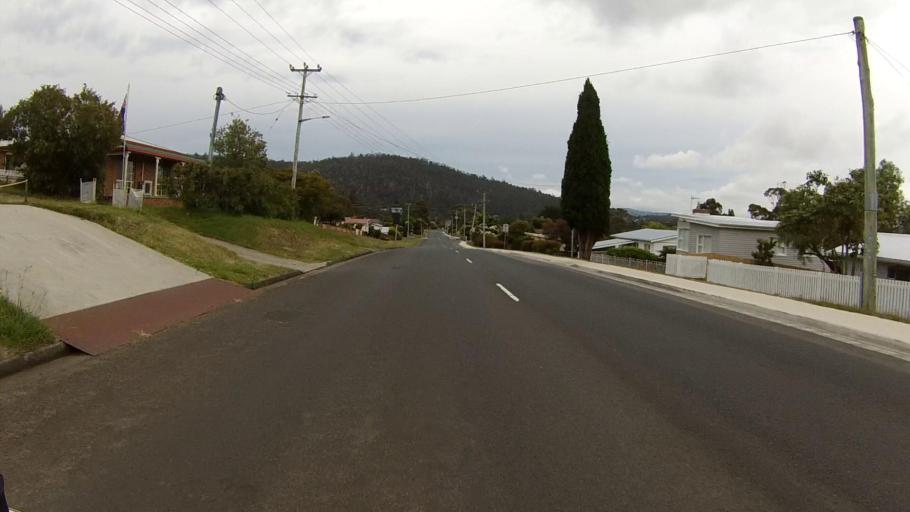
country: AU
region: Tasmania
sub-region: Sorell
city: Sorell
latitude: -42.5648
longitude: 147.8733
